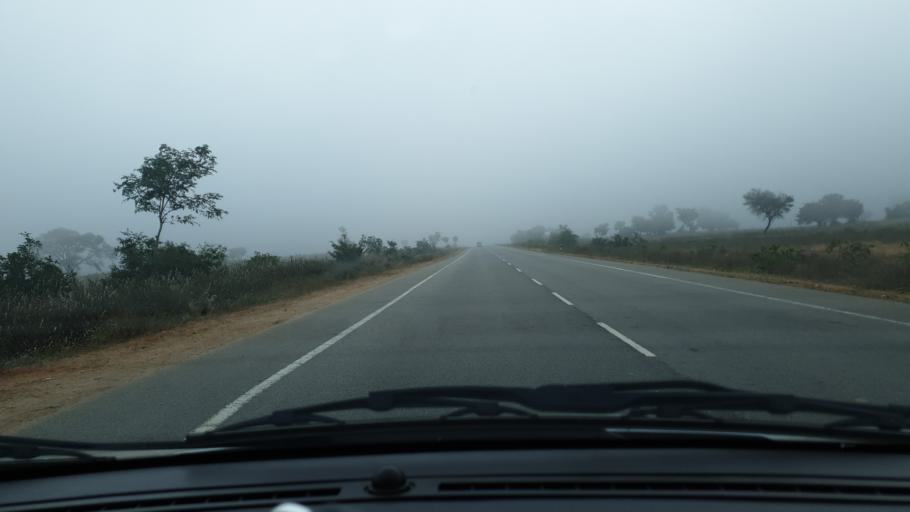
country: IN
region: Telangana
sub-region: Nalgonda
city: Devarkonda
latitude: 16.6319
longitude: 78.6589
